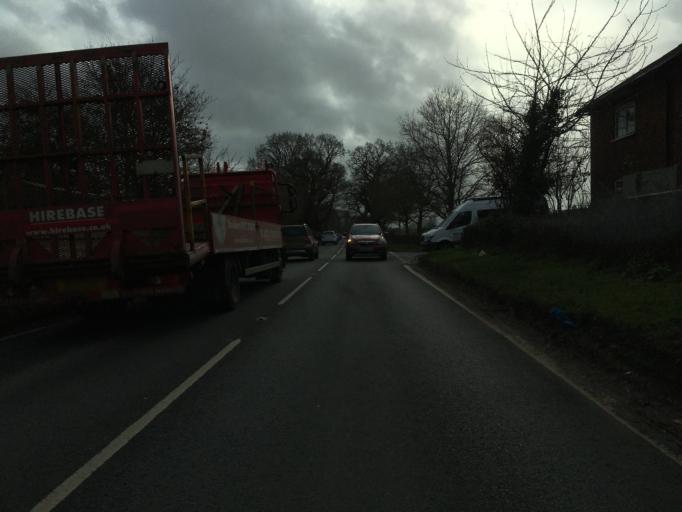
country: GB
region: England
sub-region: West Berkshire
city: Theale
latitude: 51.4520
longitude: -1.0914
